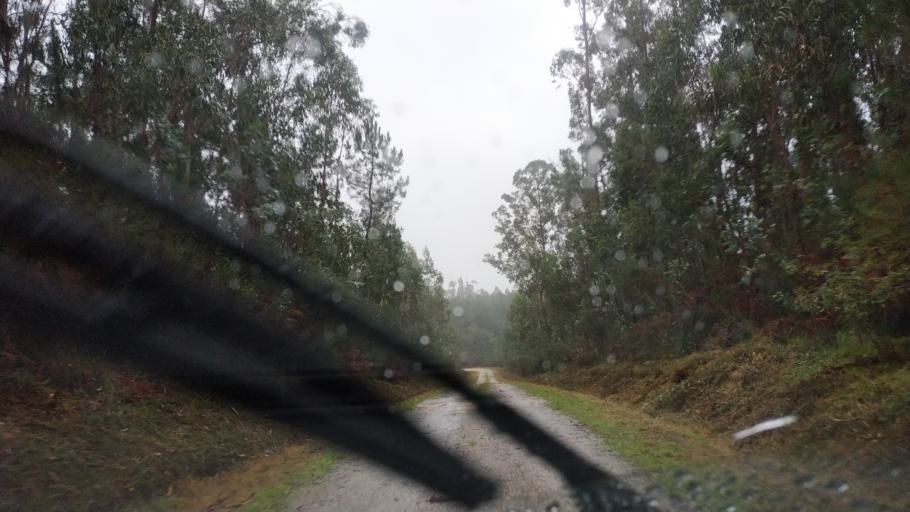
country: ES
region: Galicia
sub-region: Provincia da Coruna
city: Negreira
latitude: 42.9075
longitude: -8.7661
